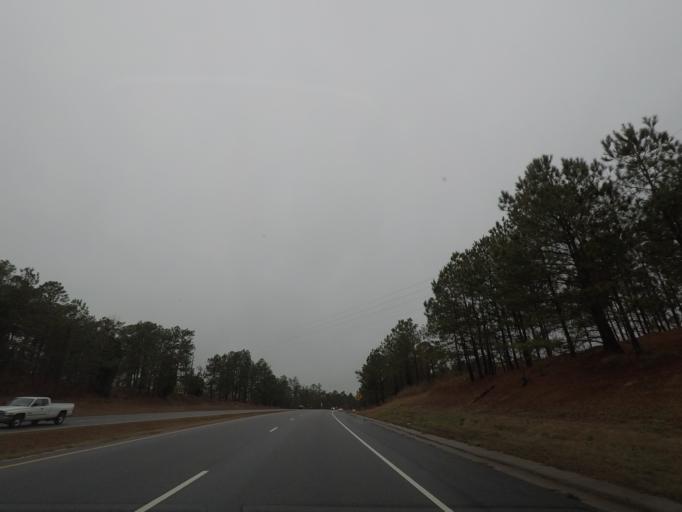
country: US
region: North Carolina
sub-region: Lee County
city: Broadway
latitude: 35.3422
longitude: -79.1035
